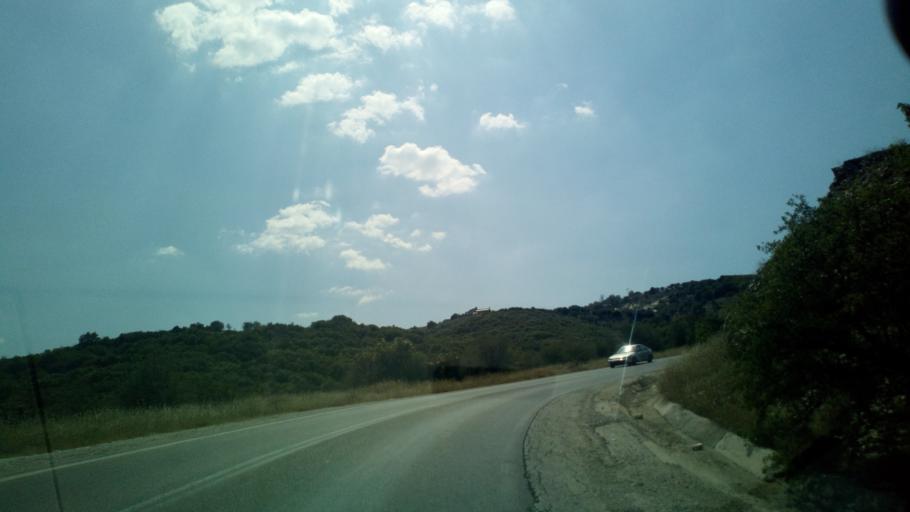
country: GR
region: Central Macedonia
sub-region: Nomos Thessalonikis
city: Chortiatis
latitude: 40.6351
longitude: 23.1027
